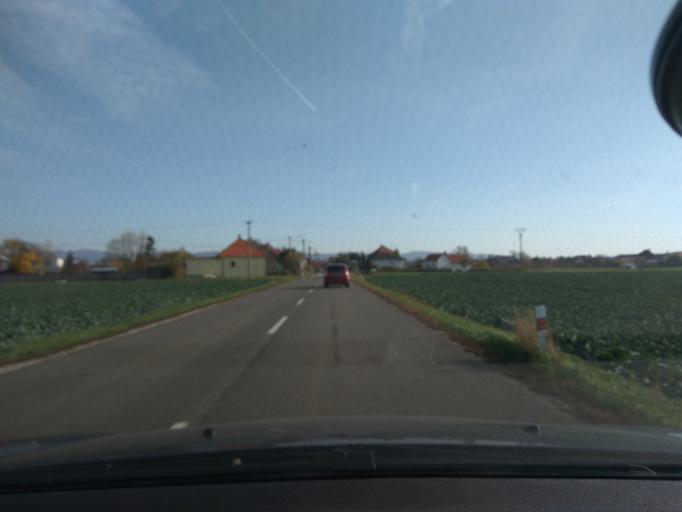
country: SK
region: Trnavsky
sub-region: Okres Trnava
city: Piestany
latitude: 48.6218
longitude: 17.7862
